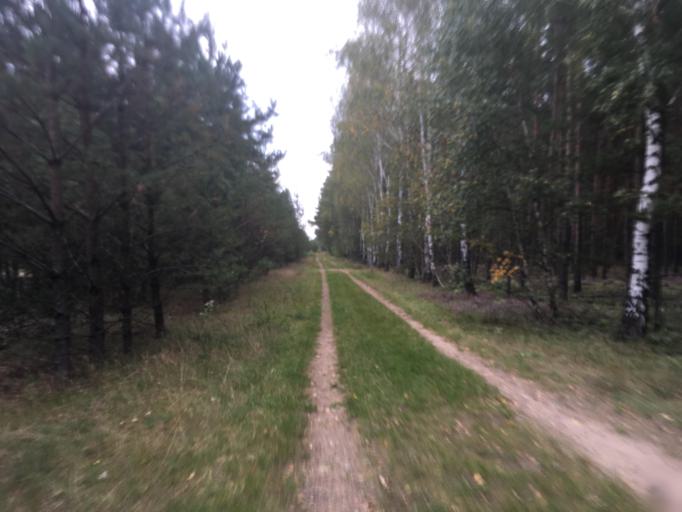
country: DE
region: Brandenburg
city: Glienicke
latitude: 52.6947
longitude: 13.3539
